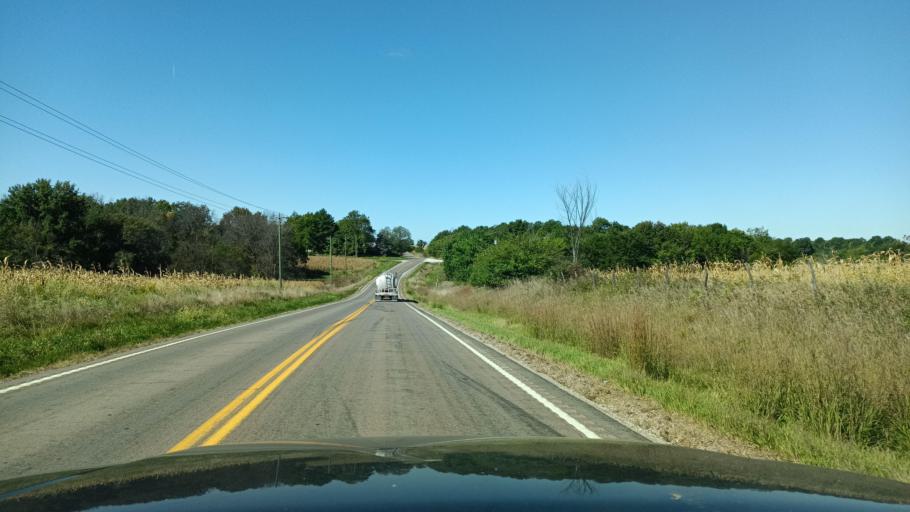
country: US
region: Missouri
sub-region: Scotland County
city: Memphis
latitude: 40.4552
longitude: -92.0543
